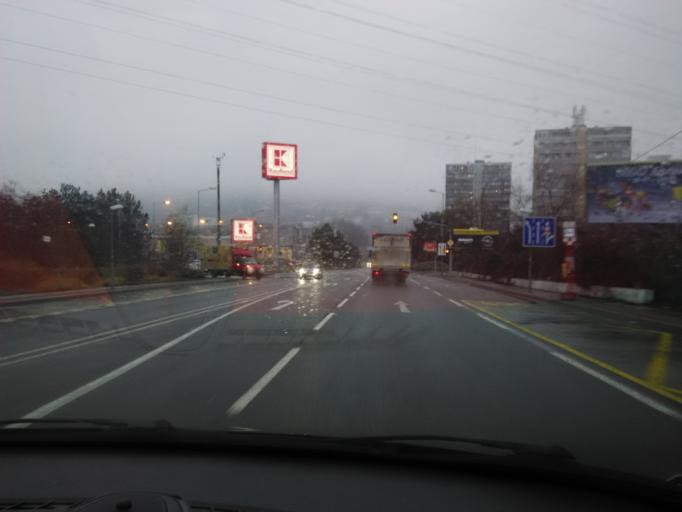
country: SK
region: Bratislavsky
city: Bratislava
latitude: 48.1791
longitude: 17.0551
